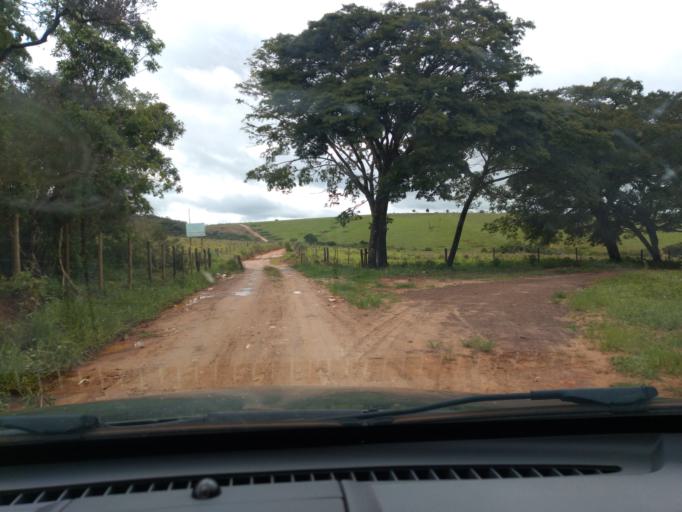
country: BR
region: Minas Gerais
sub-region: Lavras
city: Lavras
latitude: -21.5122
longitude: -44.9288
